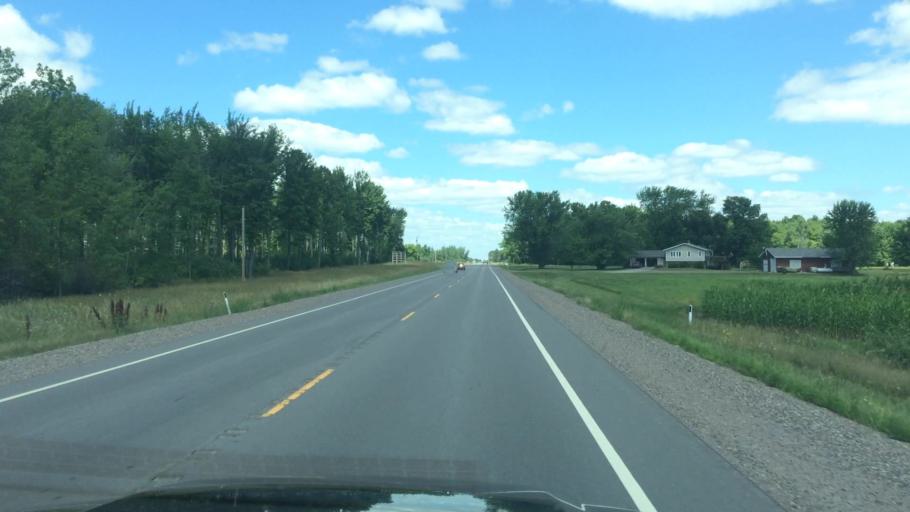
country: US
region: Wisconsin
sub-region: Clark County
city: Abbotsford
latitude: 45.0227
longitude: -90.3151
